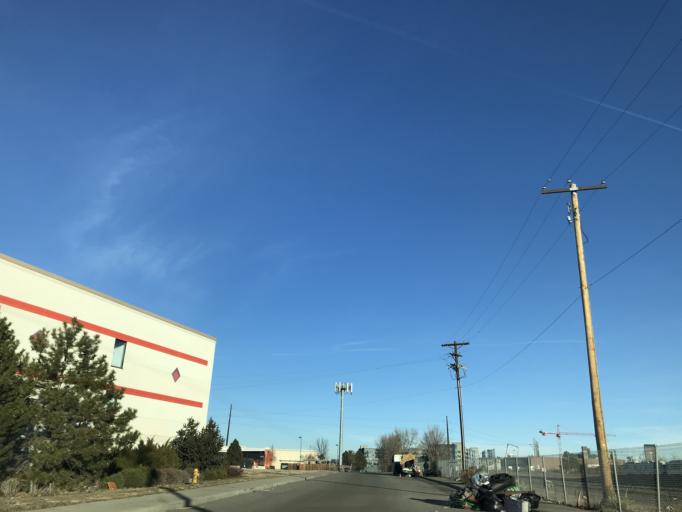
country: US
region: Colorado
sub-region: Denver County
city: Denver
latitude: 39.7045
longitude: -104.9917
